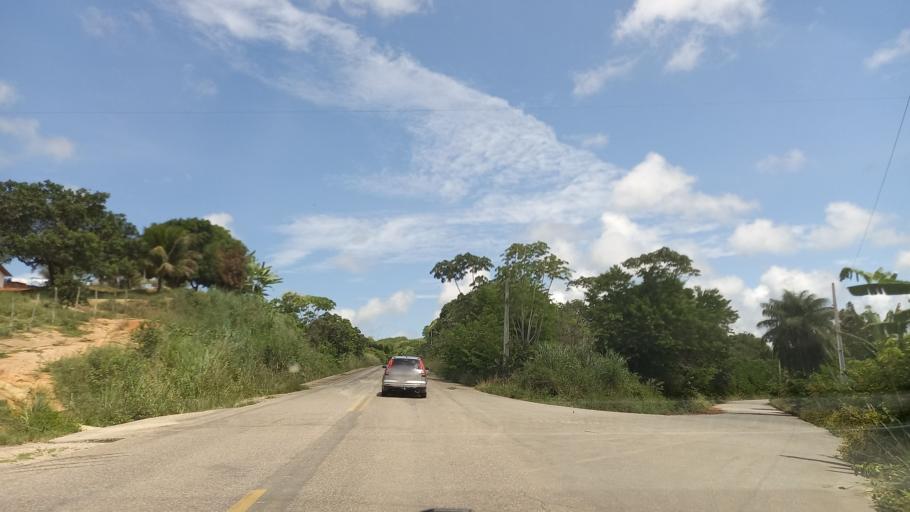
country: BR
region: Pernambuco
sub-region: Barreiros
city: Barreiros
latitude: -8.8288
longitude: -35.1769
